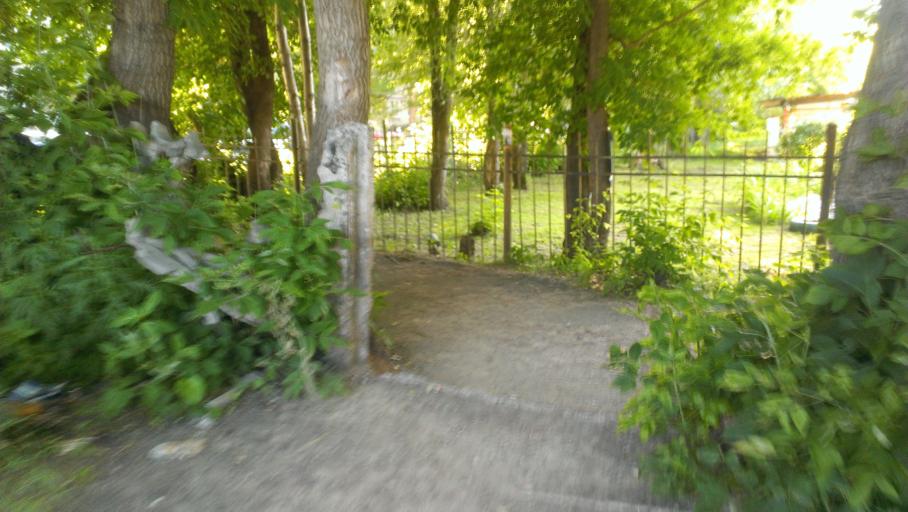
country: RU
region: Altai Krai
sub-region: Gorod Barnaulskiy
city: Barnaul
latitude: 53.3663
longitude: 83.6985
